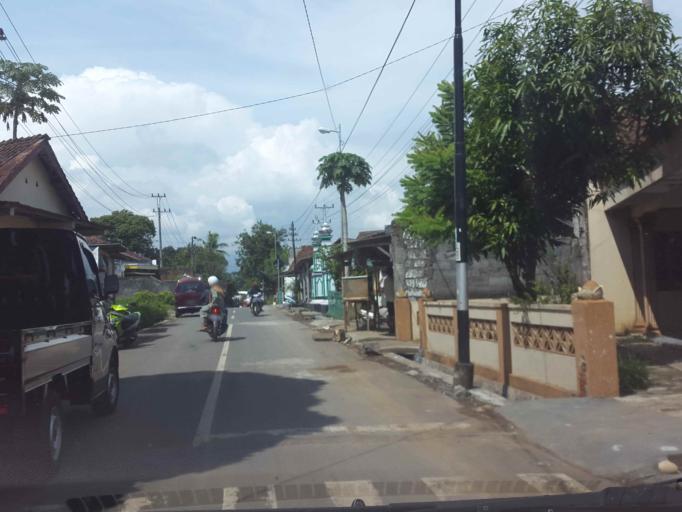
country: ID
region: Central Java
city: Salatiga
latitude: -7.3217
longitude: 110.5148
